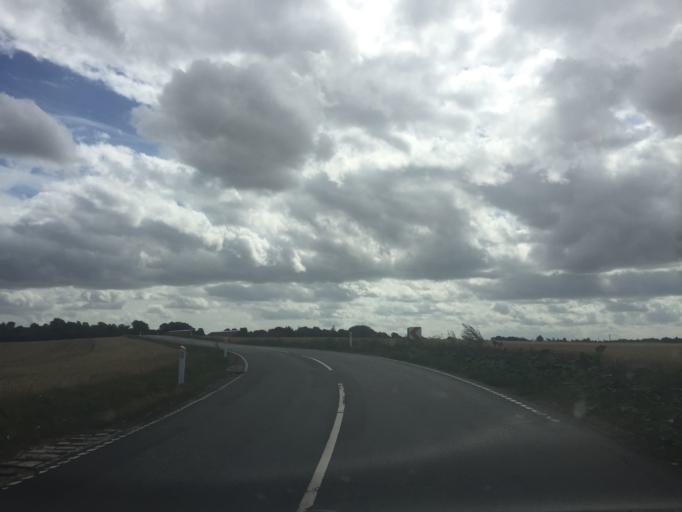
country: DK
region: Capital Region
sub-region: Hoje-Taastrup Kommune
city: Flong
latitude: 55.6956
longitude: 12.2345
